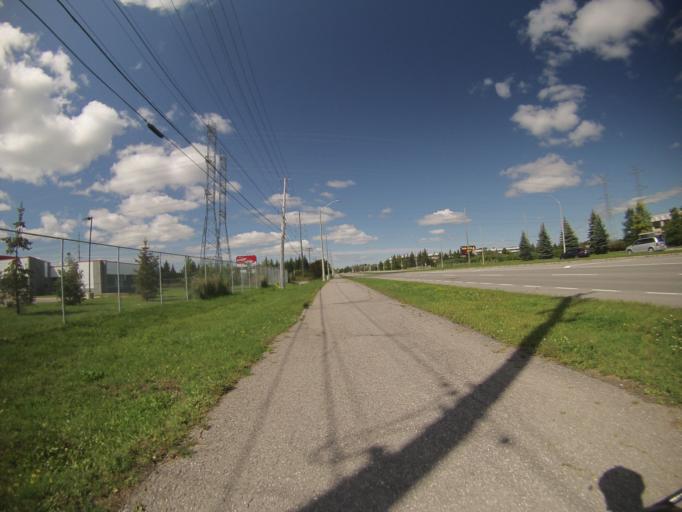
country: CA
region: Ontario
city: Ottawa
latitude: 45.3778
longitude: -75.6269
